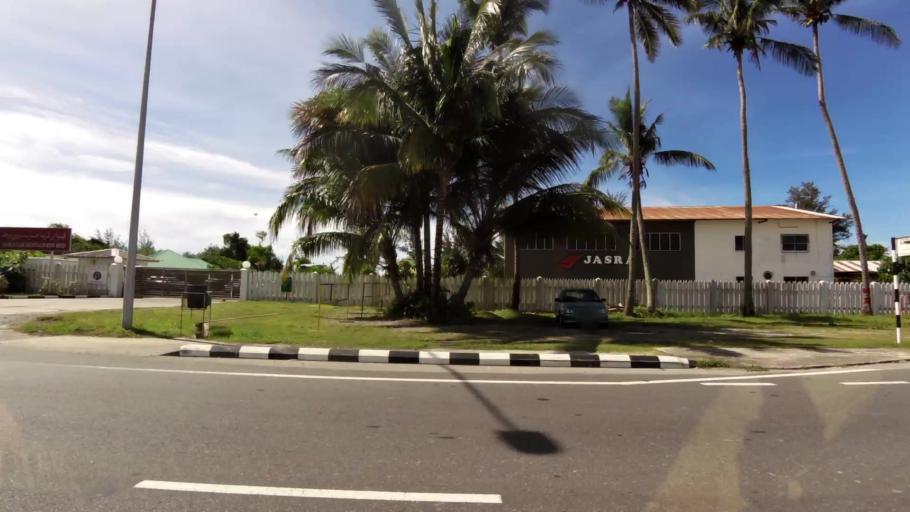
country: BN
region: Belait
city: Kuala Belait
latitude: 4.5891
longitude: 114.2059
